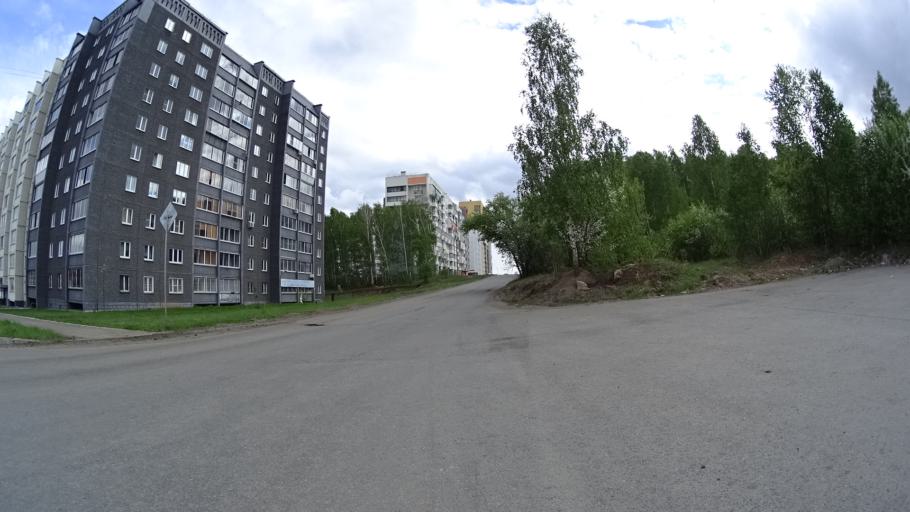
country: RU
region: Chelyabinsk
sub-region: Gorod Chelyabinsk
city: Chelyabinsk
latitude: 55.1628
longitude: 61.2859
